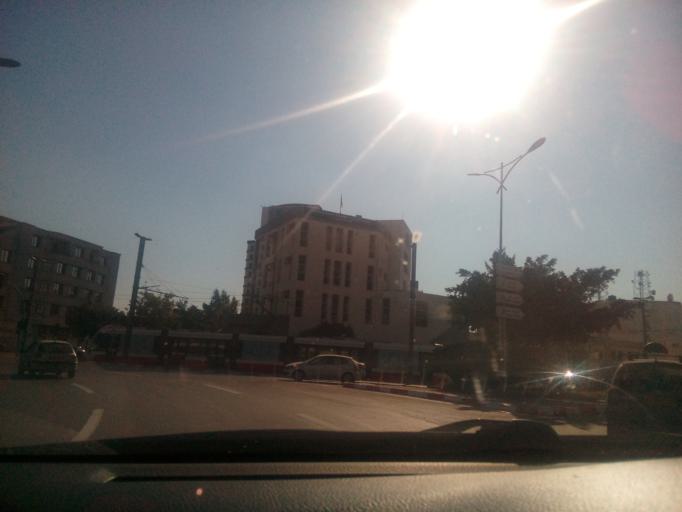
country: DZ
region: Oran
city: Oran
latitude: 35.7023
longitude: -0.5986
